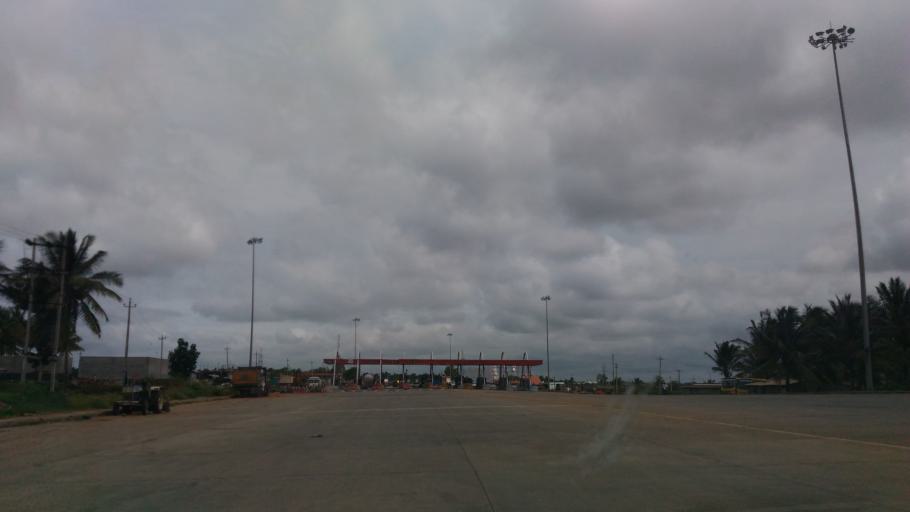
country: IN
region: Karnataka
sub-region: Hassan
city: Hassan
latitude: 12.9815
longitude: 76.2307
